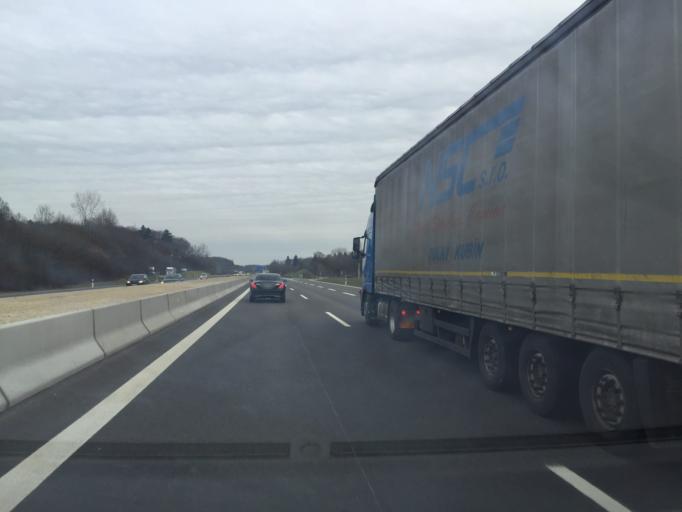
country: DE
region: Baden-Wuerttemberg
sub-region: Freiburg Region
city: Muhlhausen-Ehingen
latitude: 47.8266
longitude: 8.8307
